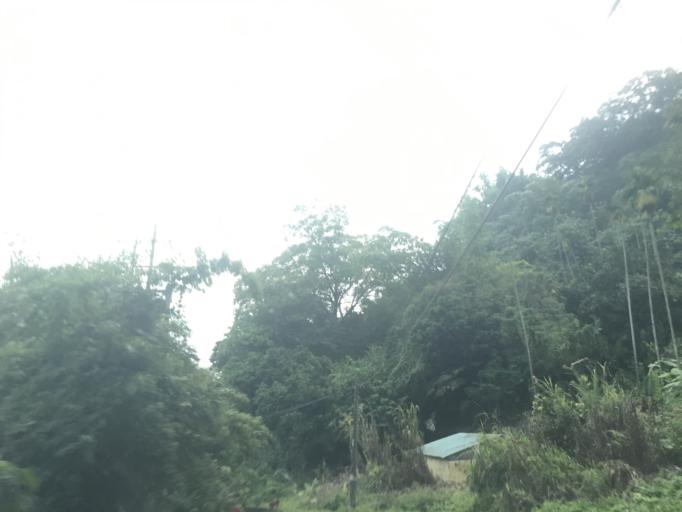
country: TW
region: Taiwan
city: Fengyuan
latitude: 24.1882
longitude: 120.7808
